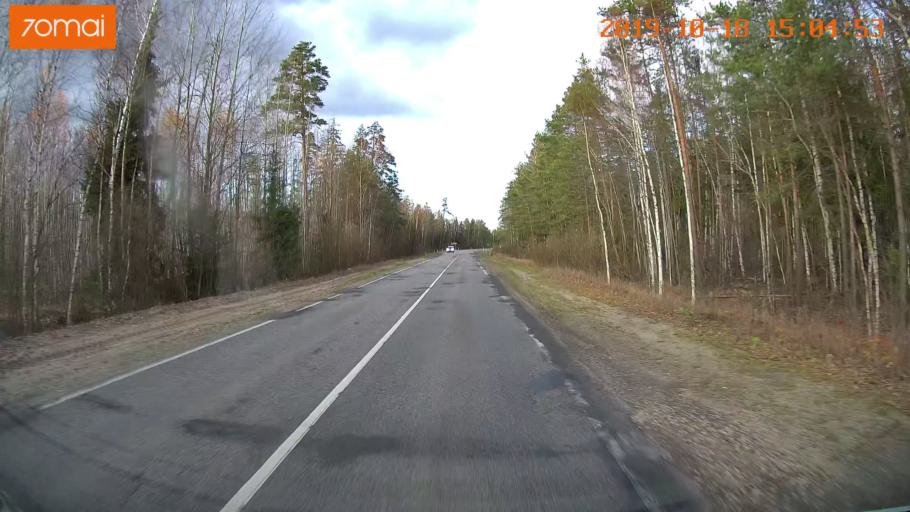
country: RU
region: Vladimir
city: Kurlovo
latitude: 55.5074
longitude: 40.5704
